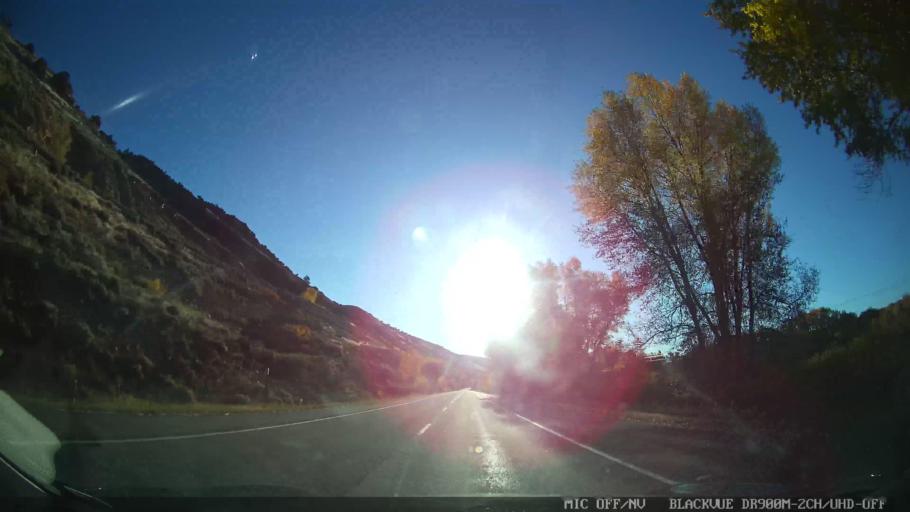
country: US
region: Colorado
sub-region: Grand County
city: Hot Sulphur Springs
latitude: 40.0647
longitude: -106.1907
